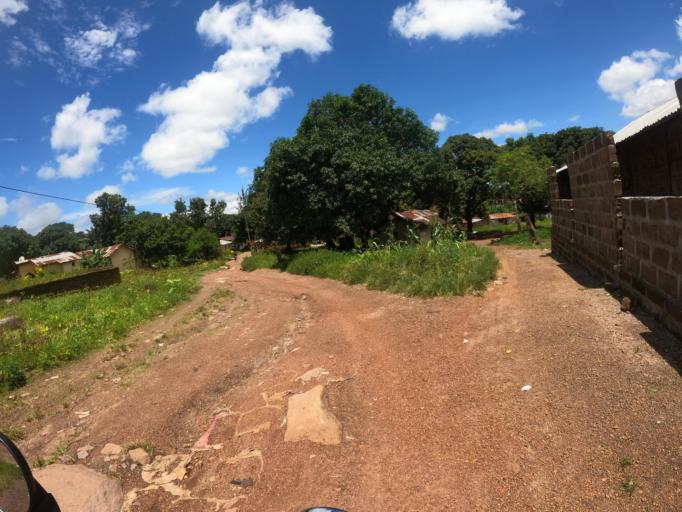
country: SL
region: Northern Province
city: Makeni
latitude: 8.8942
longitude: -12.0616
